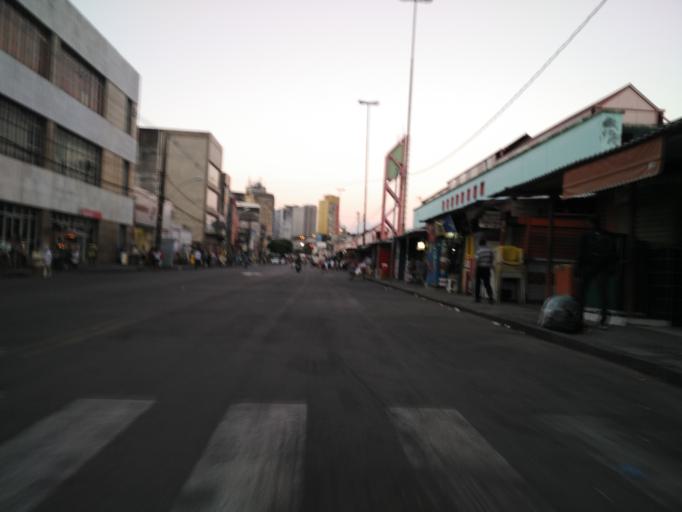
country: BR
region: Pernambuco
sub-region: Recife
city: Recife
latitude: -8.0693
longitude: -34.8817
